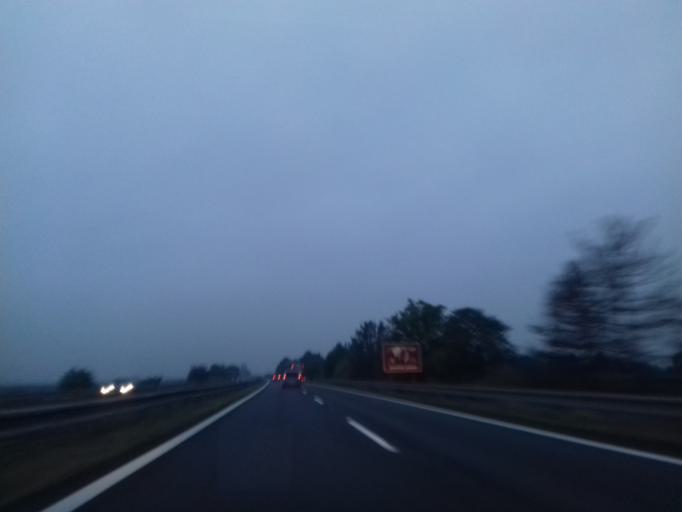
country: CZ
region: Olomoucky
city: Litovel
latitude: 49.6708
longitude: 17.0888
